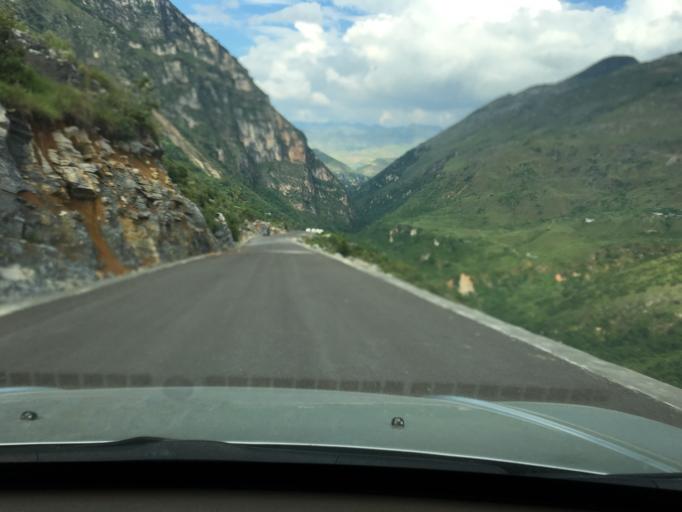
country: CN
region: Guizhou Sheng
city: Anshun
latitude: 25.7754
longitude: 105.3840
